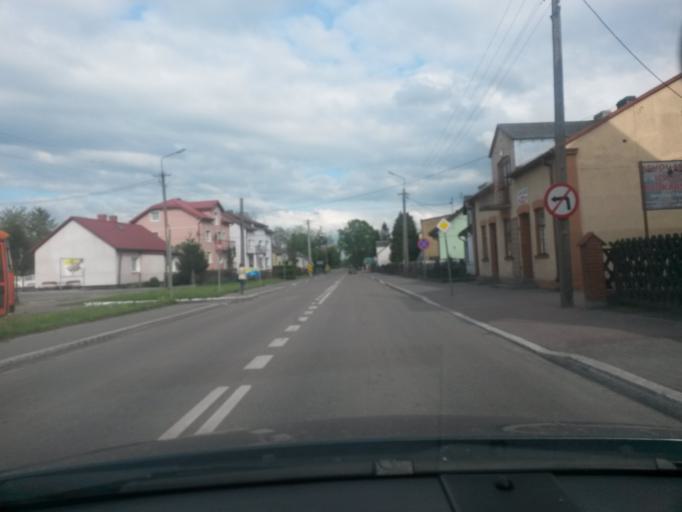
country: PL
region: Masovian Voivodeship
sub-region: Powiat sierpecki
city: Zawidz
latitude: 52.8266
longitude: 19.8764
